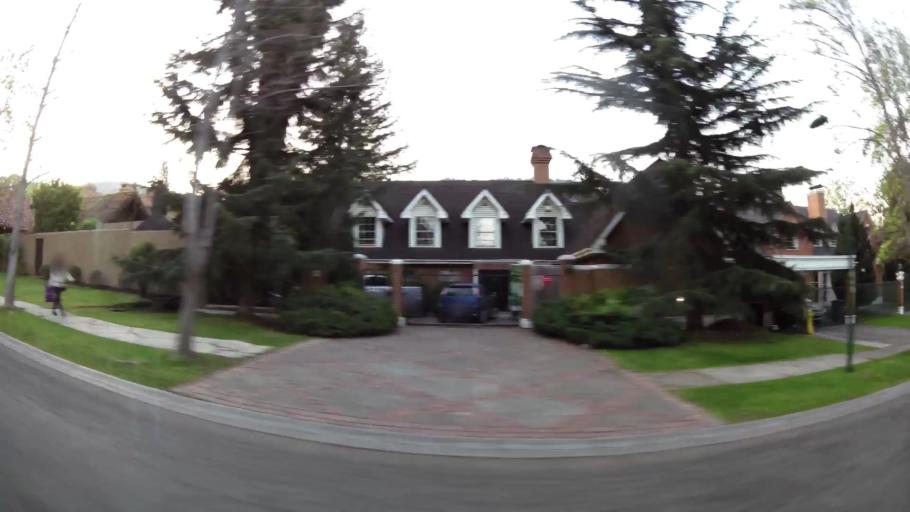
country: CL
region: Santiago Metropolitan
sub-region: Provincia de Chacabuco
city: Chicureo Abajo
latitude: -33.3396
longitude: -70.5572
